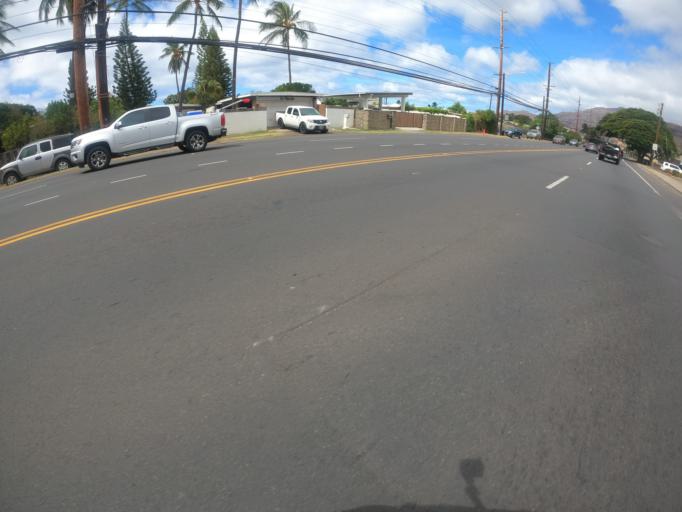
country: US
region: Hawaii
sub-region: Honolulu County
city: Waianae
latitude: 21.4372
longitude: -158.1853
